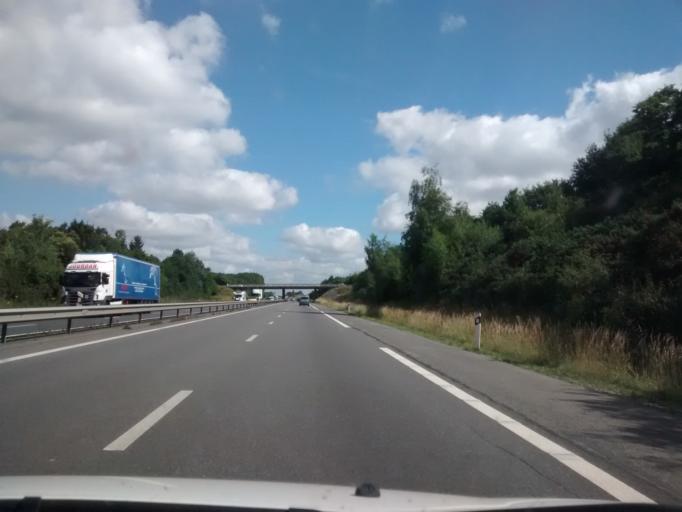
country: FR
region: Brittany
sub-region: Departement d'Ille-et-Vilaine
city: Orgeres
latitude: 48.0049
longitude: -1.6924
